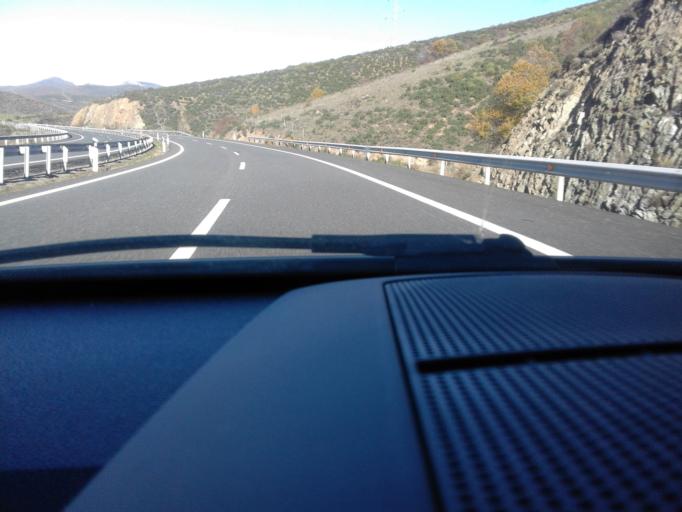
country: ES
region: Castille and Leon
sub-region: Provincia de Leon
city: Carrocera
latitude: 42.7588
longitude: -5.7732
